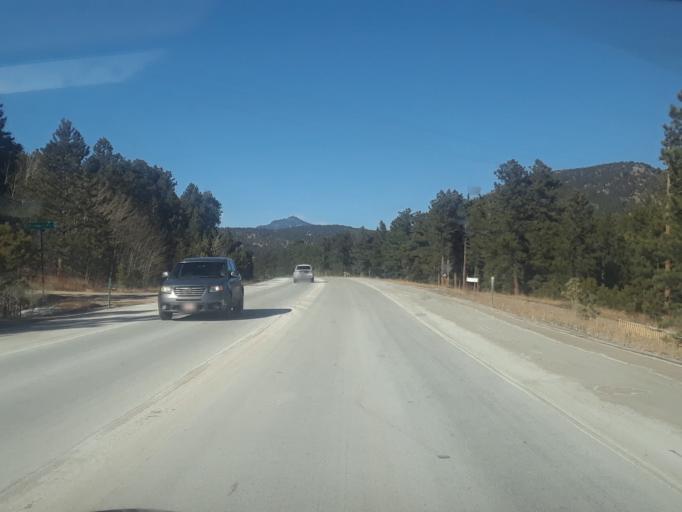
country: US
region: Colorado
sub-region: Boulder County
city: Lyons
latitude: 40.1756
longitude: -105.4698
